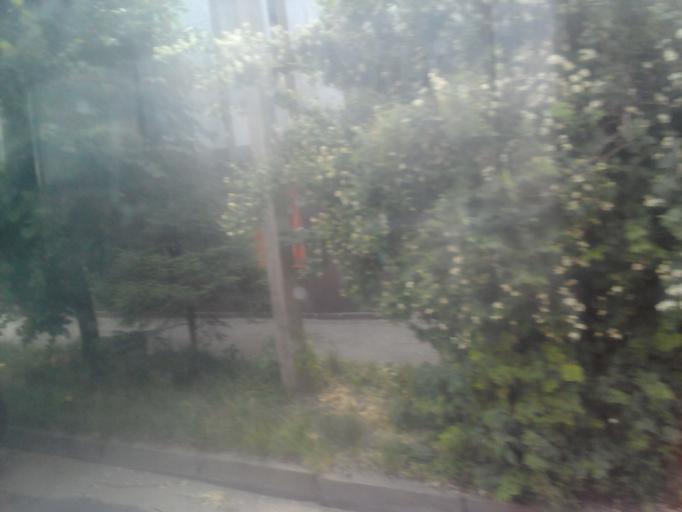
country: RU
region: Kursk
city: Kursk
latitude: 51.7341
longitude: 36.1779
